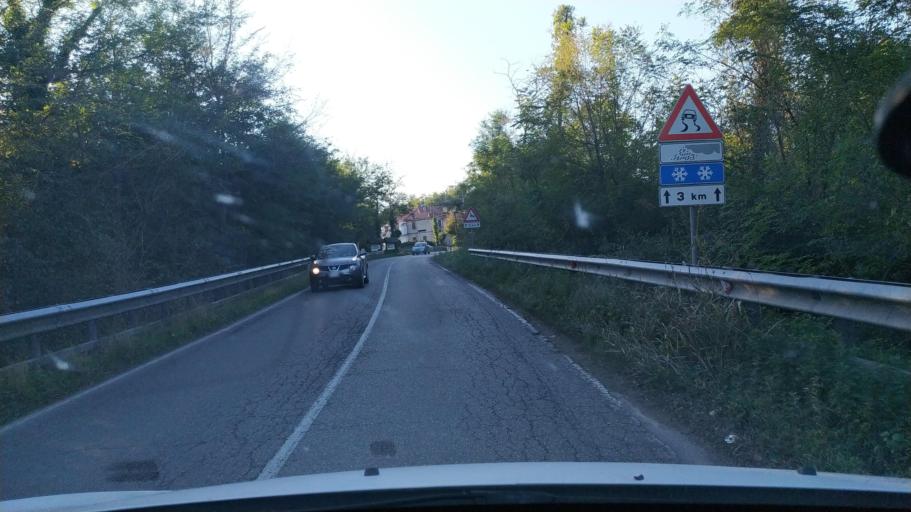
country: IT
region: Lombardy
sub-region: Provincia di Varese
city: Somma Lombardo
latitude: 45.6908
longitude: 8.6895
